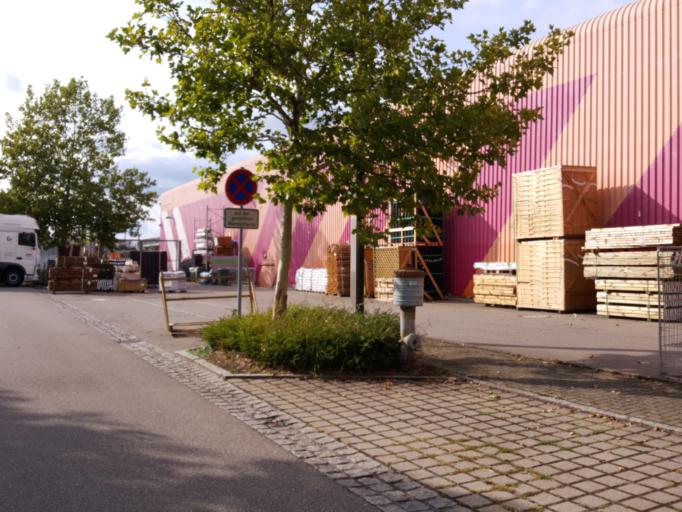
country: DE
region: Baden-Wuerttemberg
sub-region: Freiburg Region
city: Eimeldingen
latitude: 47.6247
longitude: 7.6047
